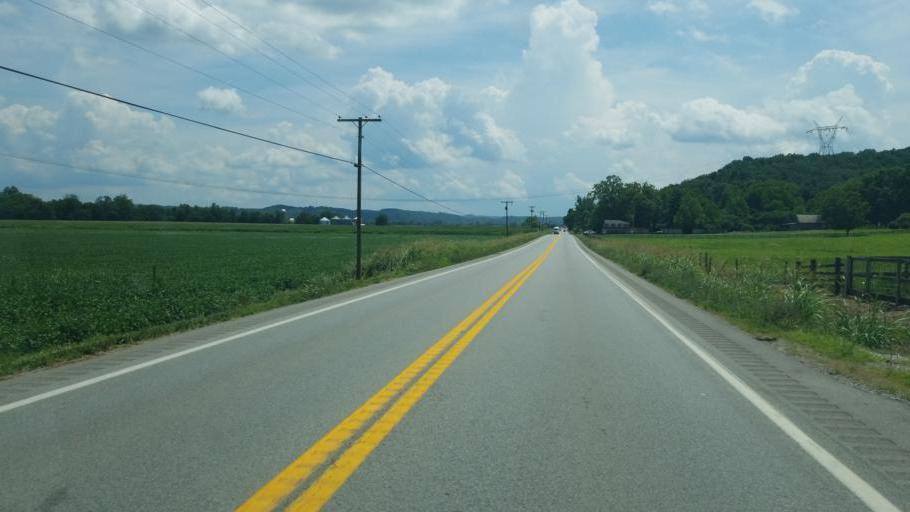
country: US
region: West Virginia
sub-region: Putnam County
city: Buffalo
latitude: 38.7475
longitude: -81.9827
